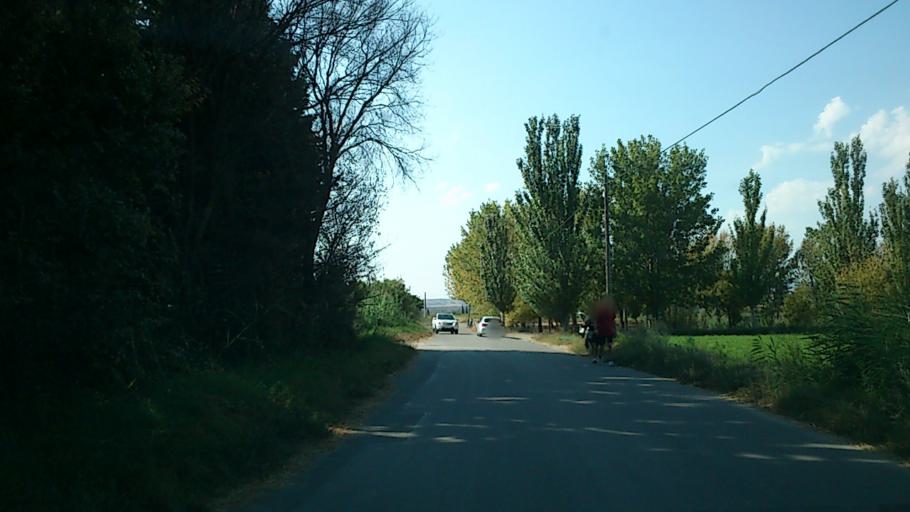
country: ES
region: Aragon
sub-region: Provincia de Zaragoza
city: Puebla de Alfinden
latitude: 41.6256
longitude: -0.7559
